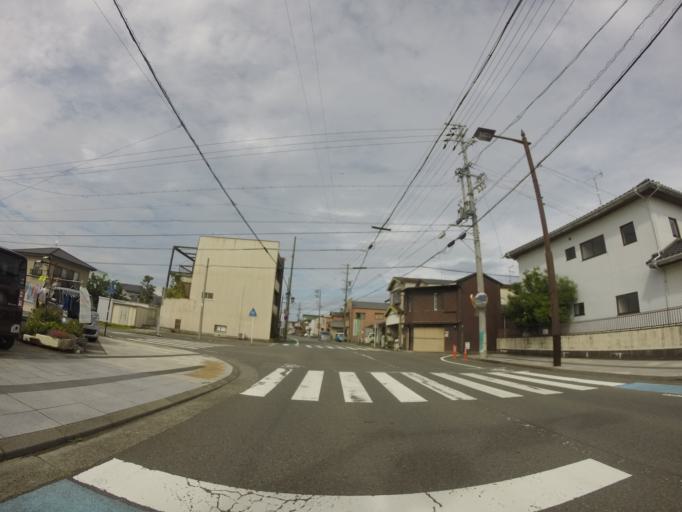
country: JP
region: Shizuoka
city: Sagara
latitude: 34.6856
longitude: 138.2008
